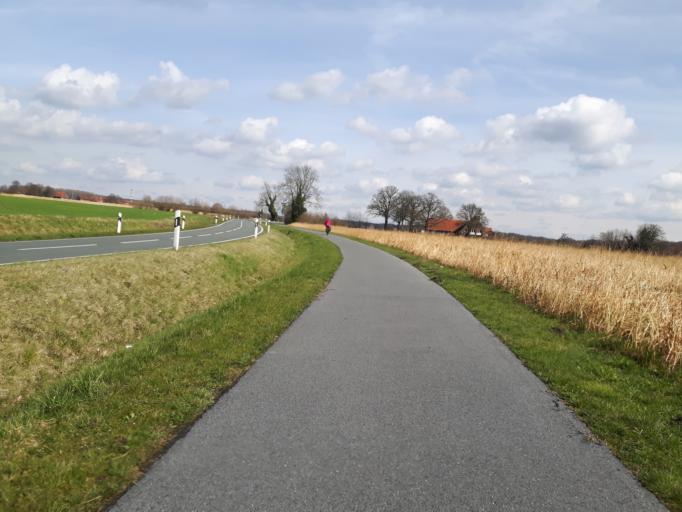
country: DE
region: North Rhine-Westphalia
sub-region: Regierungsbezirk Munster
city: Senden
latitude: 51.8410
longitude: 7.4396
